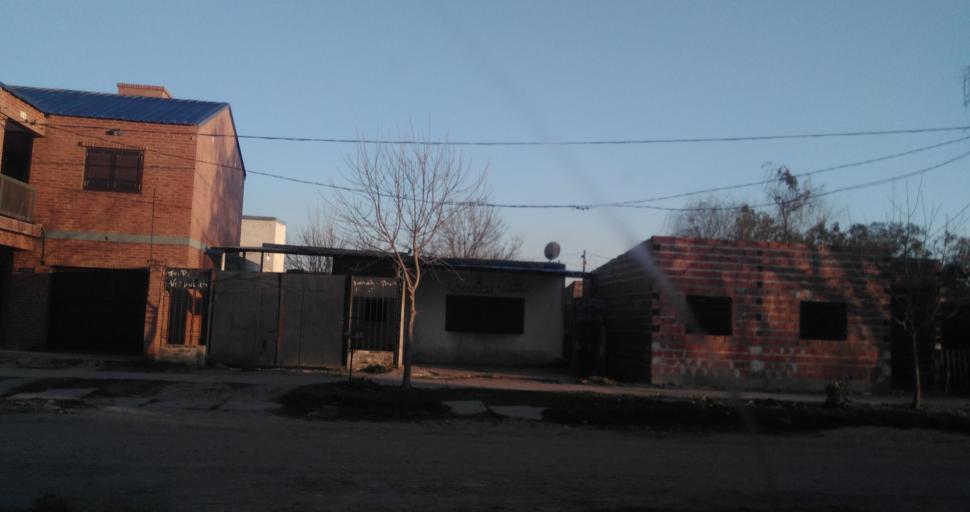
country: AR
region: Chaco
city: Resistencia
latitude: -27.4740
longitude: -59.0136
